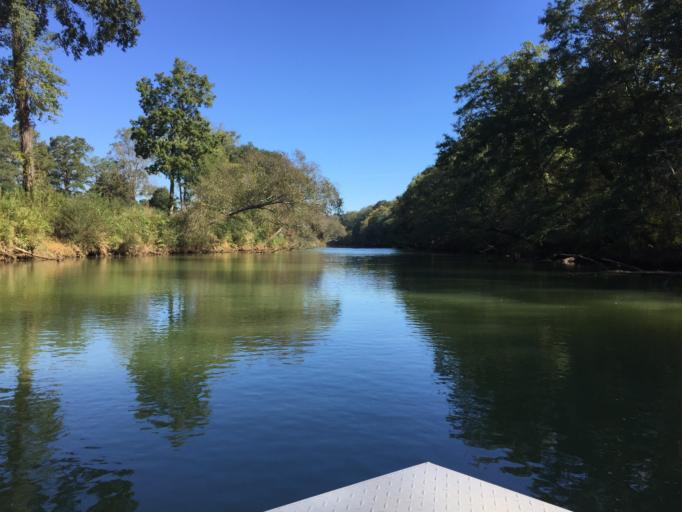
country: US
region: Georgia
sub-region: Gwinnett County
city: Berkeley Lake
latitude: 33.9948
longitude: -84.1847
